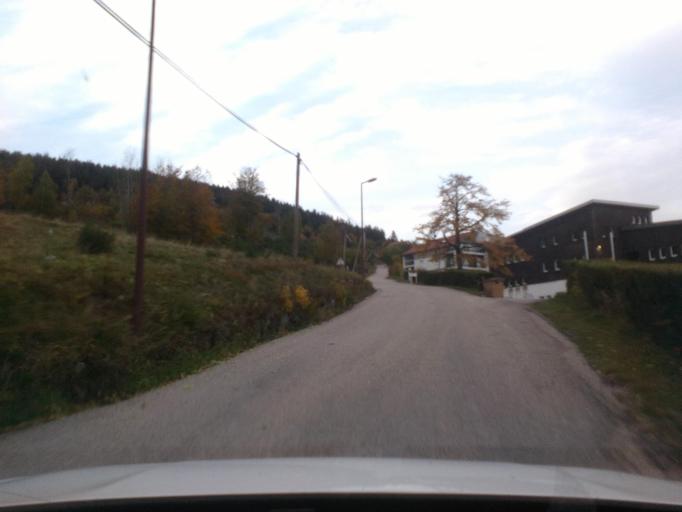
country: FR
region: Lorraine
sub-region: Departement des Vosges
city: Gerardmer
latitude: 48.0779
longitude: 6.8714
